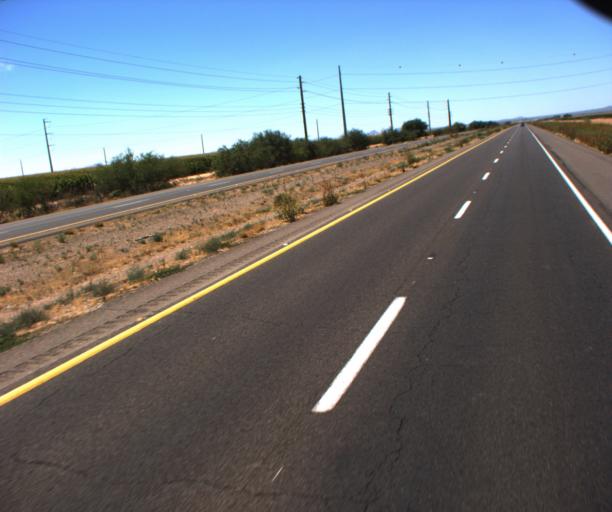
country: US
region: Arizona
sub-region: Pinal County
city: Maricopa
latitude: 32.9672
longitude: -112.0479
